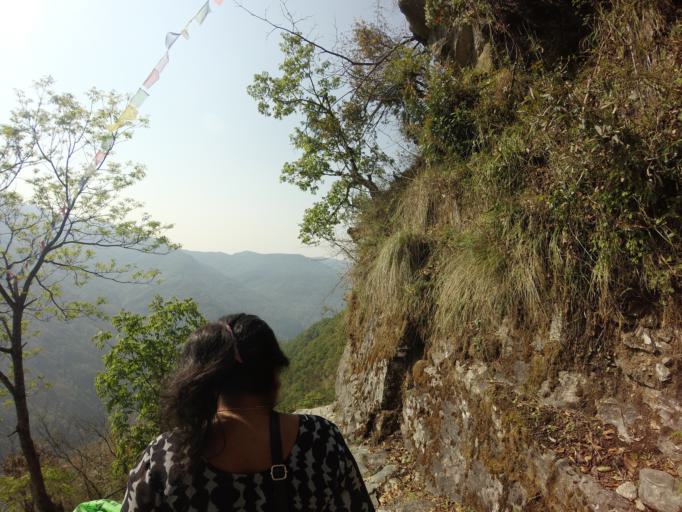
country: NP
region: Western Region
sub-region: Dhawalagiri Zone
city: Chitre
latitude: 28.3726
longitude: 83.8103
